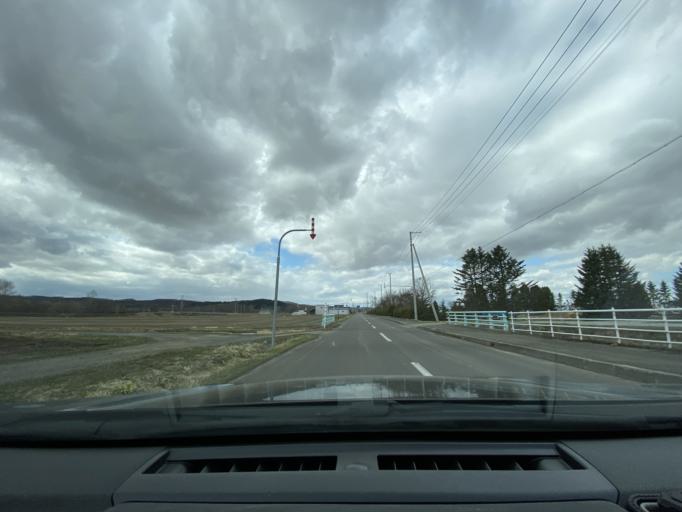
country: JP
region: Hokkaido
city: Nayoro
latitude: 44.1303
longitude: 142.4893
